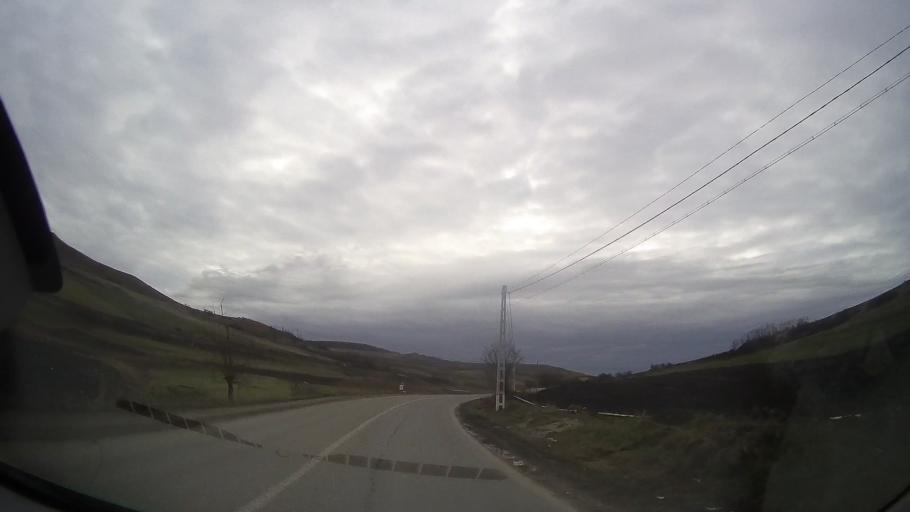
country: RO
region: Bistrita-Nasaud
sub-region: Comuna Budesti
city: Budesti
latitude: 46.8561
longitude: 24.2434
